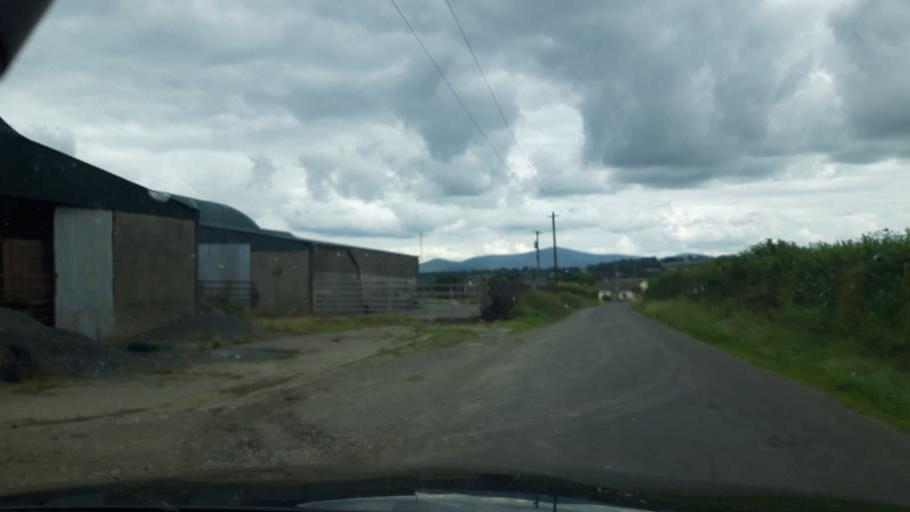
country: IE
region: Leinster
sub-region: Kilkenny
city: Graiguenamanagh
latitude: 52.6042
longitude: -7.0272
